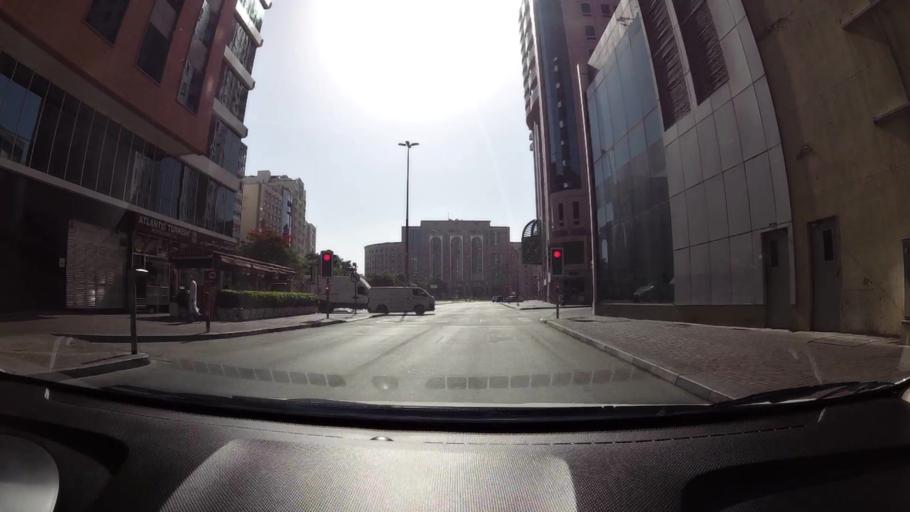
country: AE
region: Ash Shariqah
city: Sharjah
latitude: 25.2687
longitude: 55.3050
